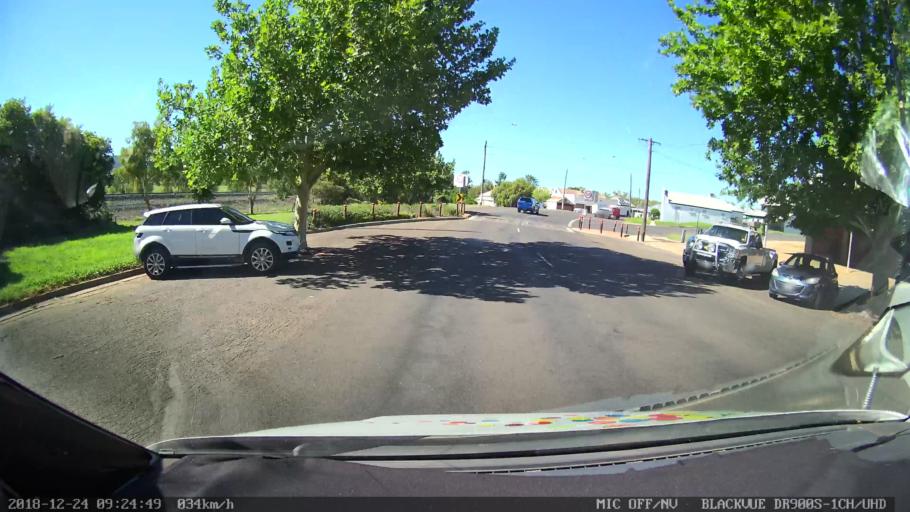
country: AU
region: New South Wales
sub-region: Liverpool Plains
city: Quirindi
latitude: -31.5117
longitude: 150.6793
